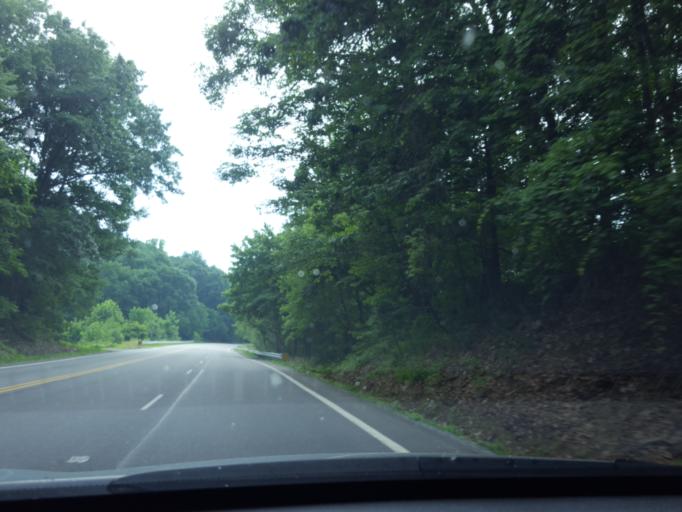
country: US
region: Virginia
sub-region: City of Waynesboro
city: Waynesboro
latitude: 38.0424
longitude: -78.8573
